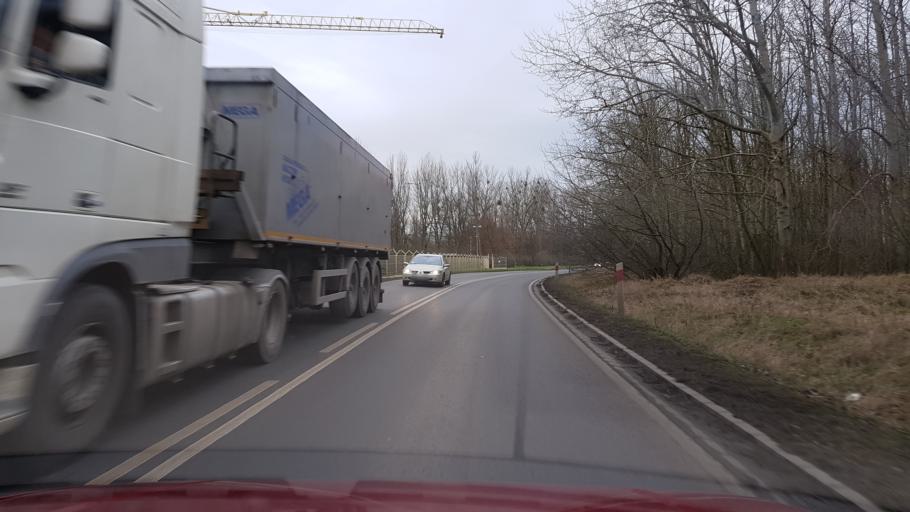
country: PL
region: West Pomeranian Voivodeship
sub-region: Powiat policki
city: Police
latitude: 53.5675
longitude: 14.5578
